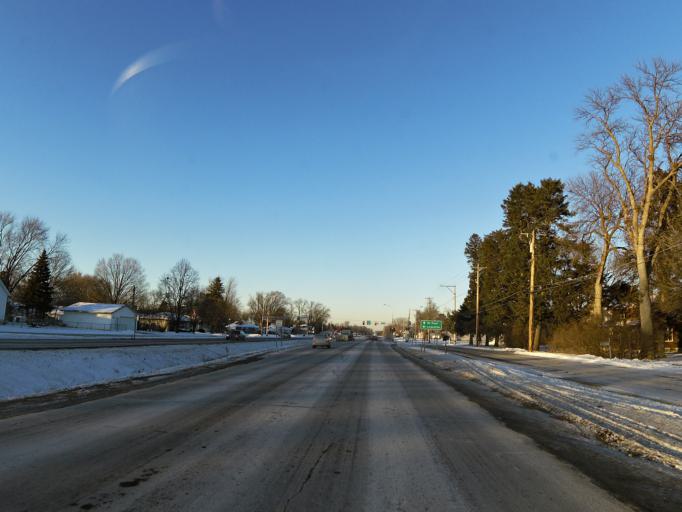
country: US
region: Minnesota
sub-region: Dakota County
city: Farmington
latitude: 44.6389
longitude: -93.1369
